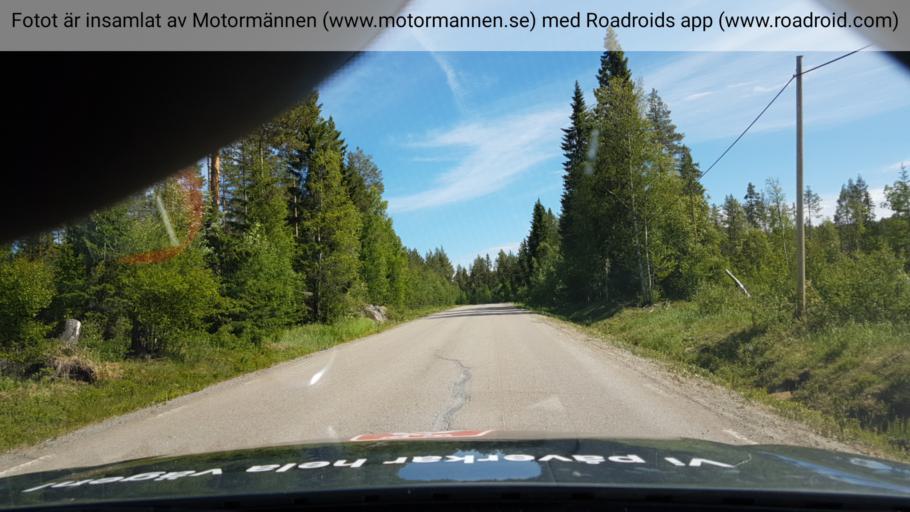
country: SE
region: Jaemtland
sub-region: Bergs Kommun
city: Hoverberg
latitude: 62.6629
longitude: 14.7654
